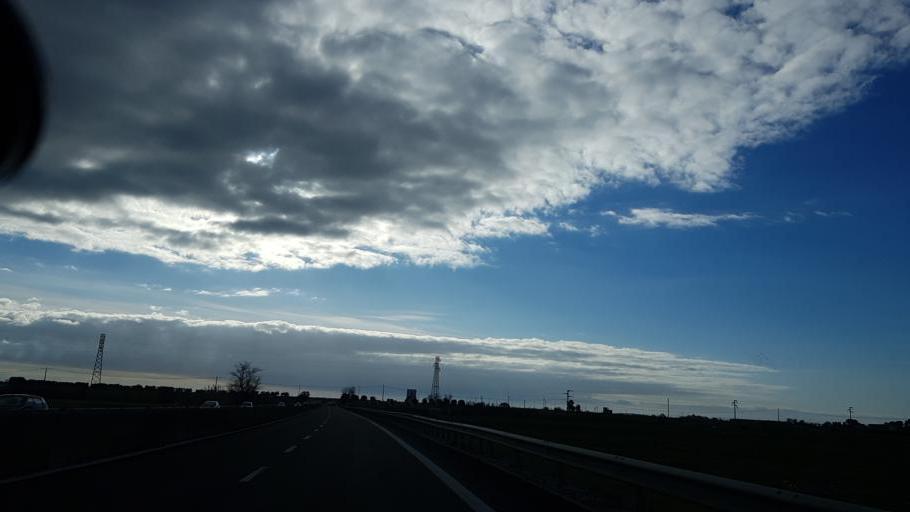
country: IT
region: Apulia
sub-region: Provincia di Brindisi
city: La Rosa
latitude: 40.5993
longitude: 17.9669
